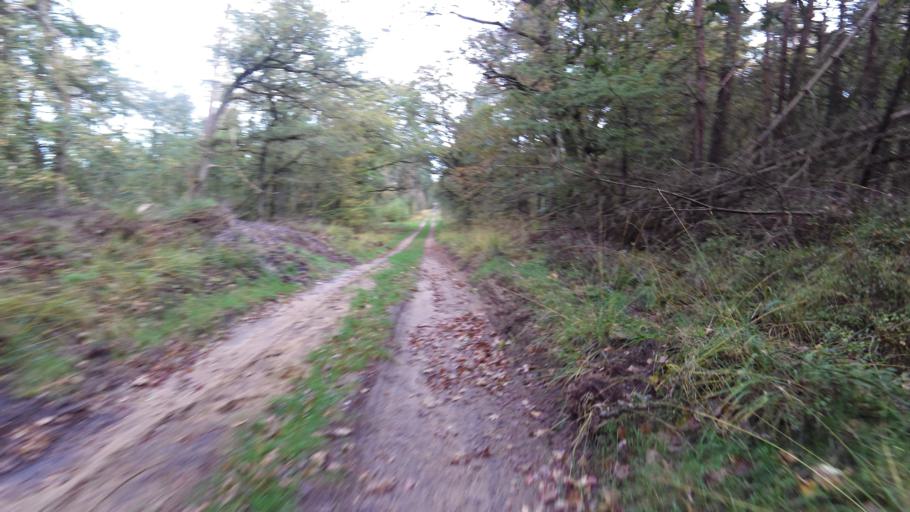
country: NL
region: Gelderland
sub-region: Gemeente Nunspeet
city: Nunspeet
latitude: 52.3172
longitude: 5.8623
